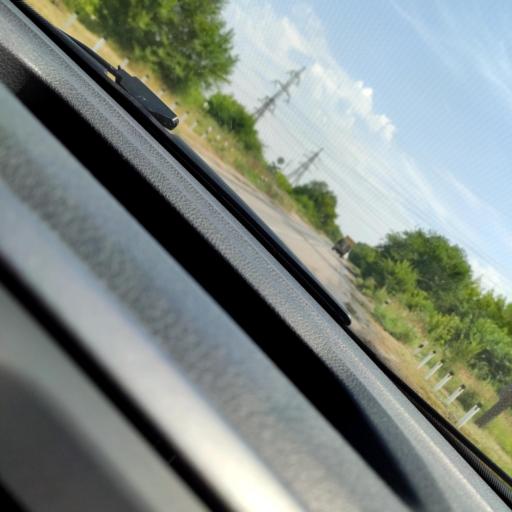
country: RU
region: Samara
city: Tol'yatti
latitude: 53.5803
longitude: 49.2588
